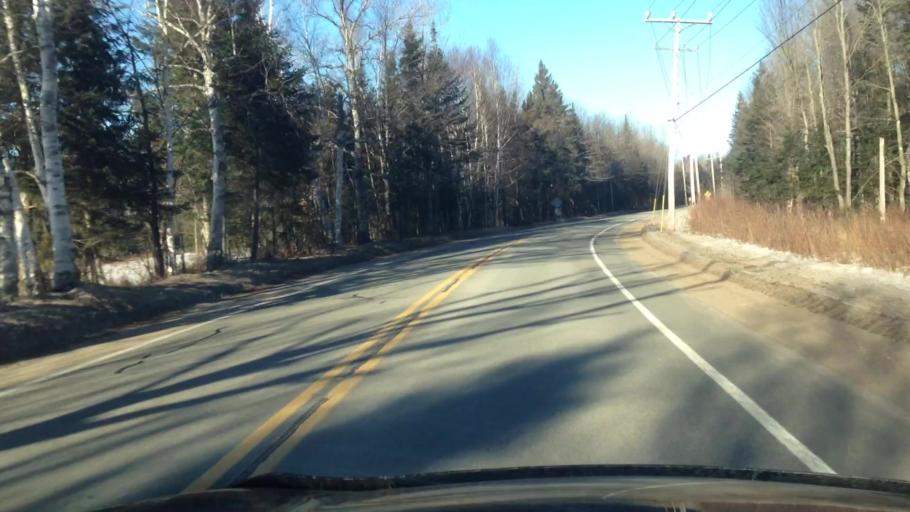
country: CA
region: Quebec
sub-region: Laurentides
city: Mont-Tremblant
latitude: 46.0126
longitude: -74.6149
